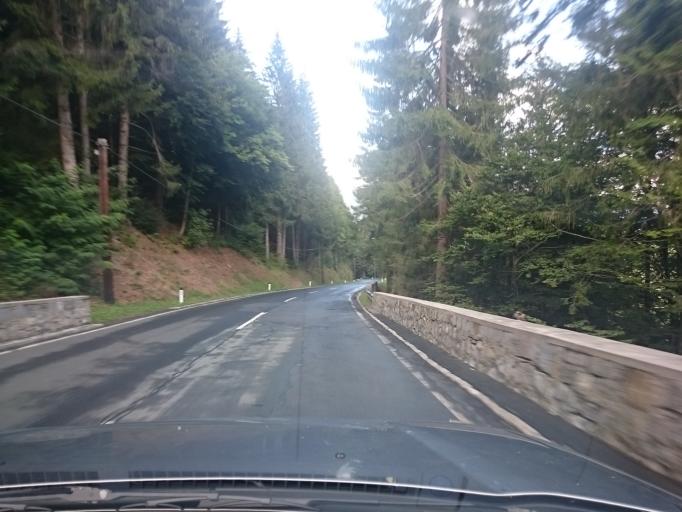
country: AT
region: Carinthia
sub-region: Politischer Bezirk Spittal an der Drau
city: Oberdrauburg
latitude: 46.6530
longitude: 12.9763
